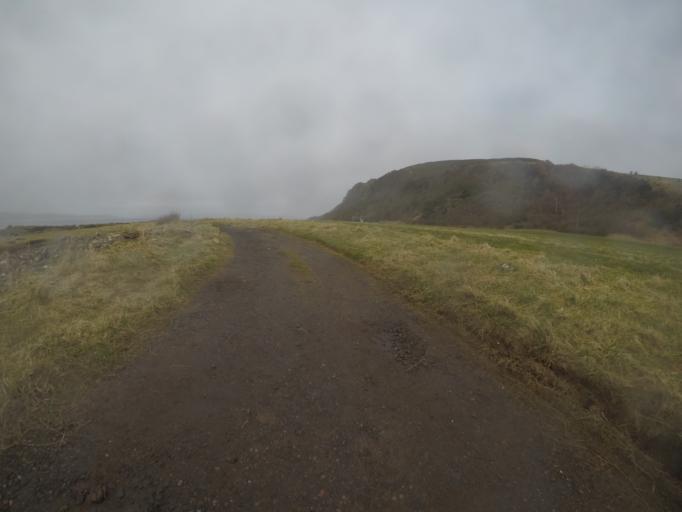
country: GB
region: Scotland
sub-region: North Ayrshire
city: Millport
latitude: 55.7036
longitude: -4.9040
